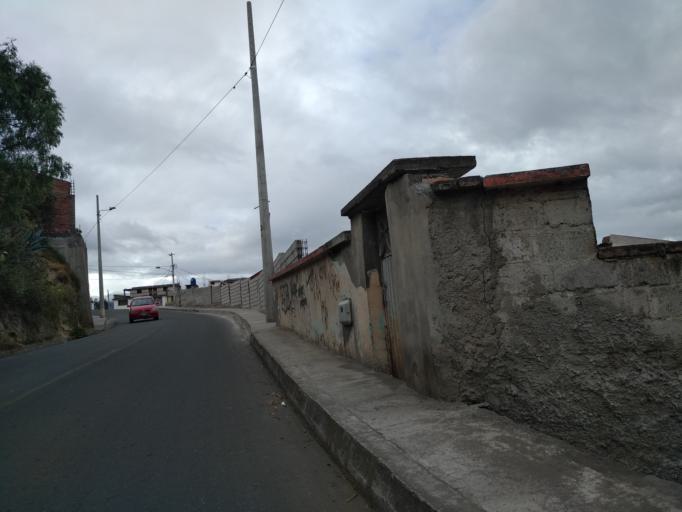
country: EC
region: Chimborazo
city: Riobamba
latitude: -1.6857
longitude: -78.6794
